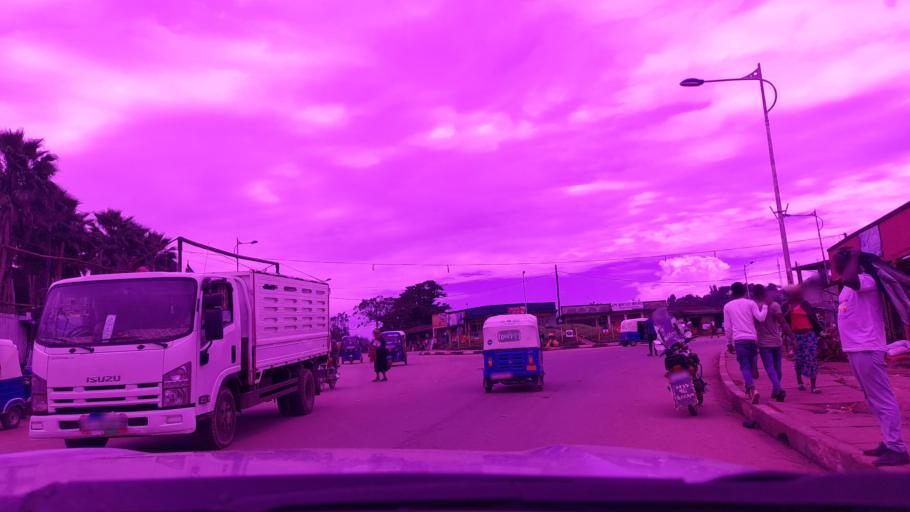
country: ET
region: Southern Nations, Nationalities, and People's Region
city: Mizan Teferi
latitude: 6.9938
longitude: 35.5935
